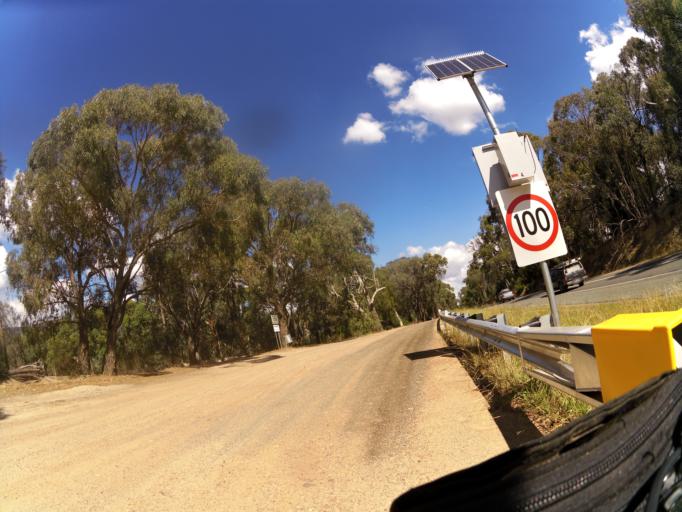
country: AU
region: Victoria
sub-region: Mansfield
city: Mansfield
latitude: -36.8399
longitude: 146.0074
